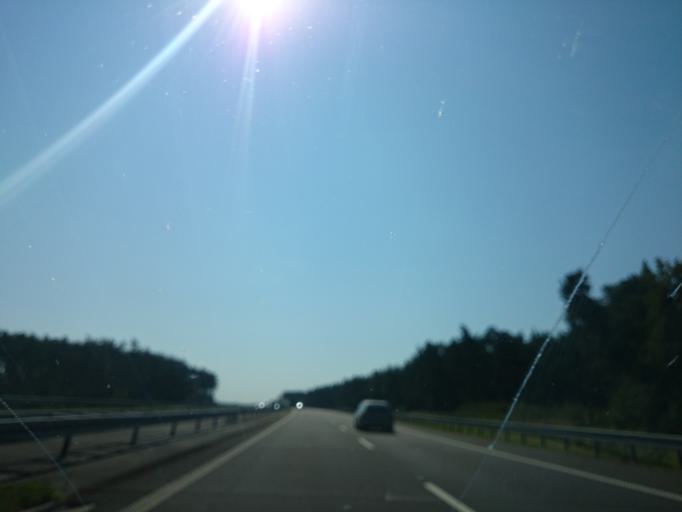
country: PL
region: West Pomeranian Voivodeship
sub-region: Powiat pyrzycki
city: Bielice
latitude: 53.2173
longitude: 14.6528
